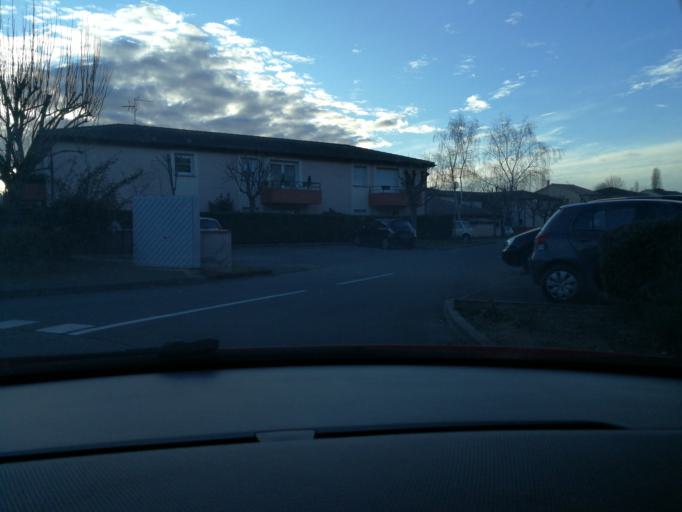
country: FR
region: Midi-Pyrenees
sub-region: Departement de la Haute-Garonne
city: Balma
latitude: 43.6073
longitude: 1.4930
